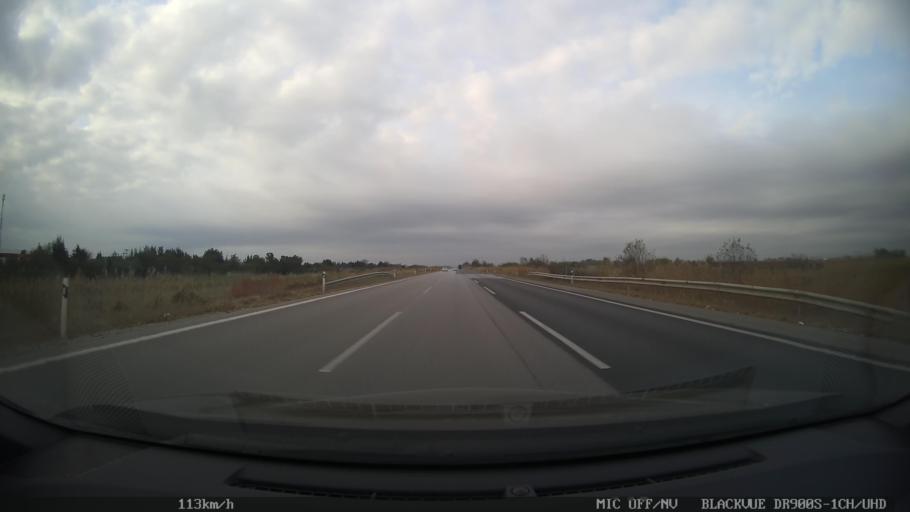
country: GR
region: Central Macedonia
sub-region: Nomos Thessalonikis
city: Chalastra
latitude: 40.6323
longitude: 22.7783
